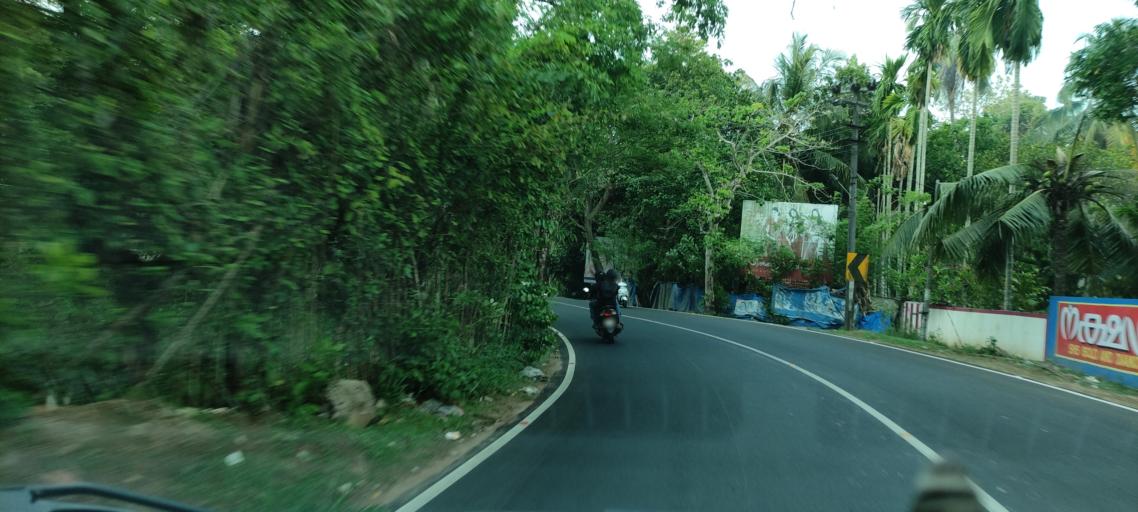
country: IN
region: Kerala
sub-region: Alappuzha
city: Arukutti
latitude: 9.8359
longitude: 76.3329
